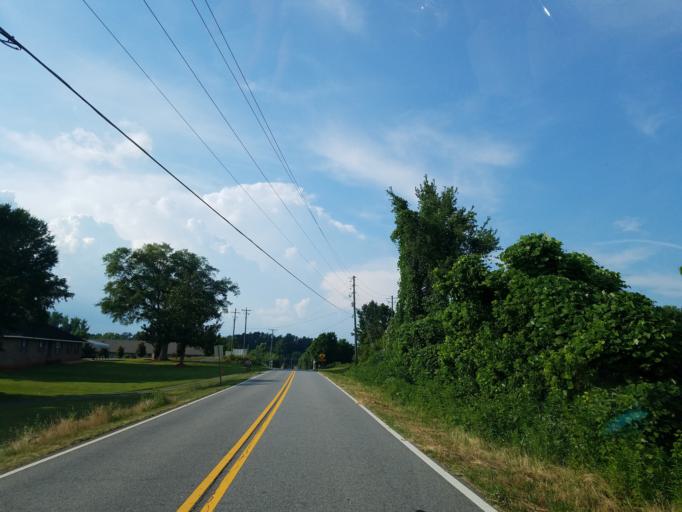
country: US
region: Georgia
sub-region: Forsyth County
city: Cumming
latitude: 34.3007
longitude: -84.0667
